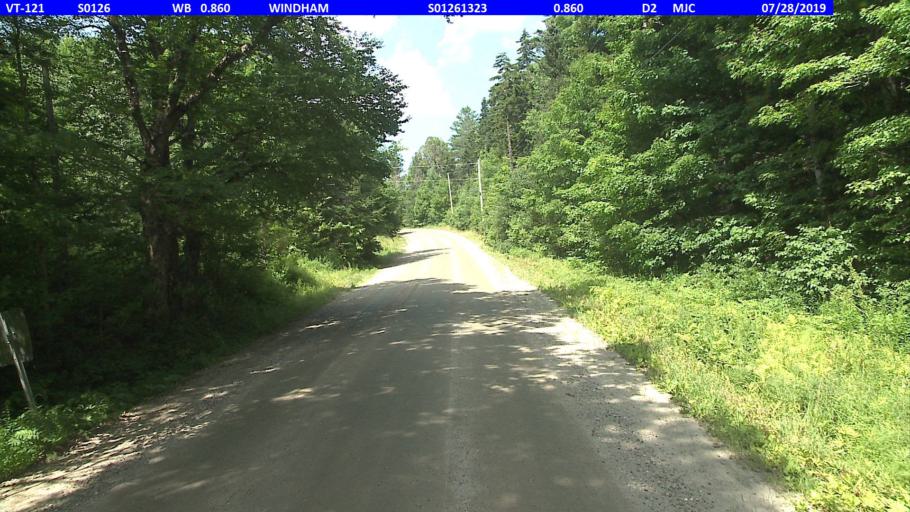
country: US
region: Vermont
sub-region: Windsor County
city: Chester
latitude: 43.1981
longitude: -72.7038
